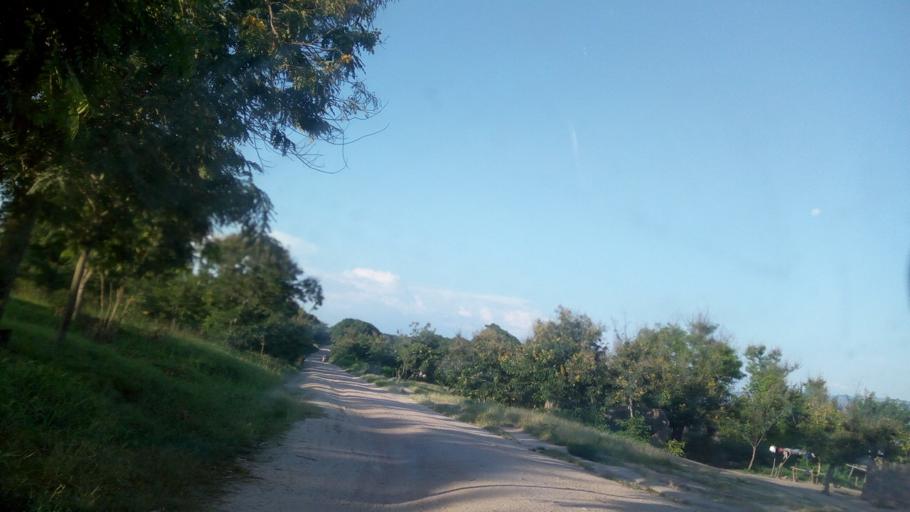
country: BI
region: Bururi
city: Rumonge
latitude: -4.1676
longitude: 29.0619
